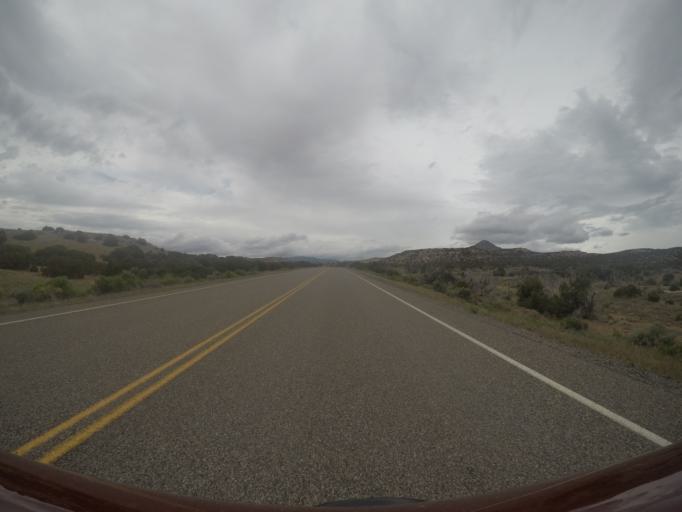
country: US
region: Wyoming
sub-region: Big Horn County
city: Lovell
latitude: 44.9992
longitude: -108.2637
